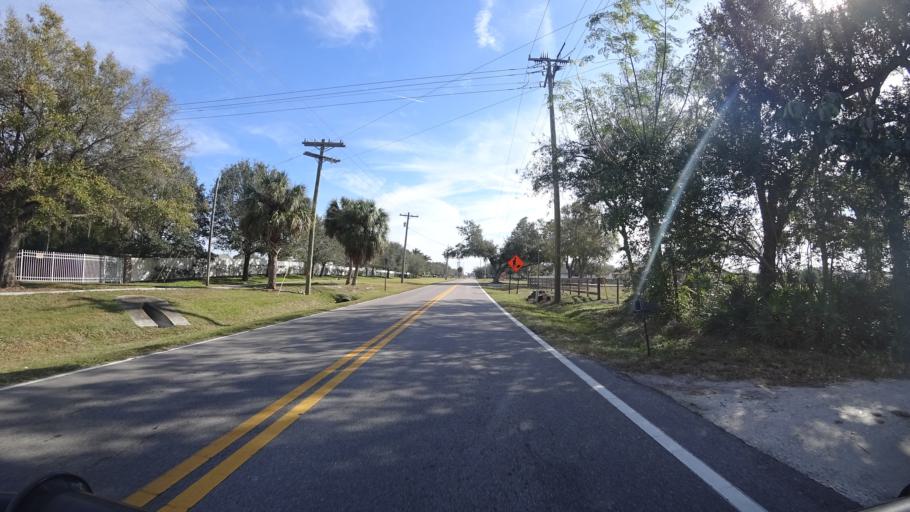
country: US
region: Florida
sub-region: Manatee County
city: Memphis
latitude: 27.5756
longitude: -82.5322
